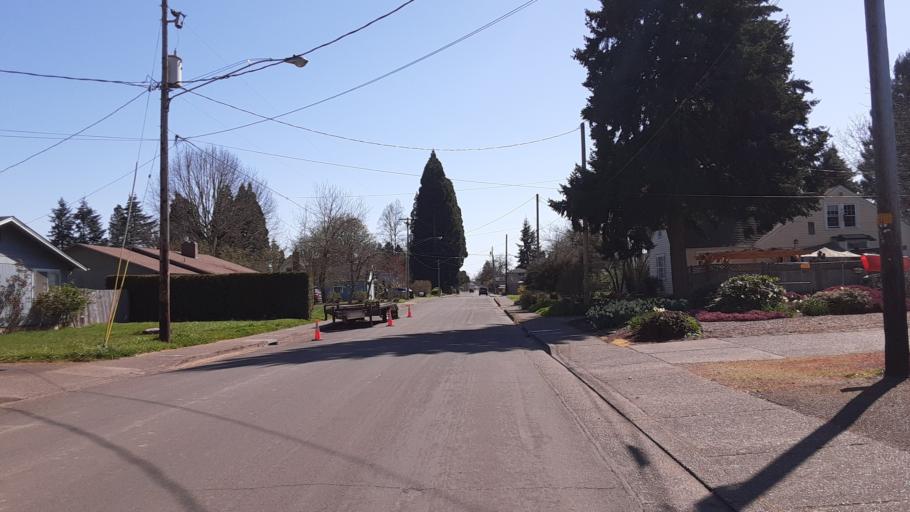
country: US
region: Oregon
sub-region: Benton County
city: Corvallis
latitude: 44.5446
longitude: -123.2605
